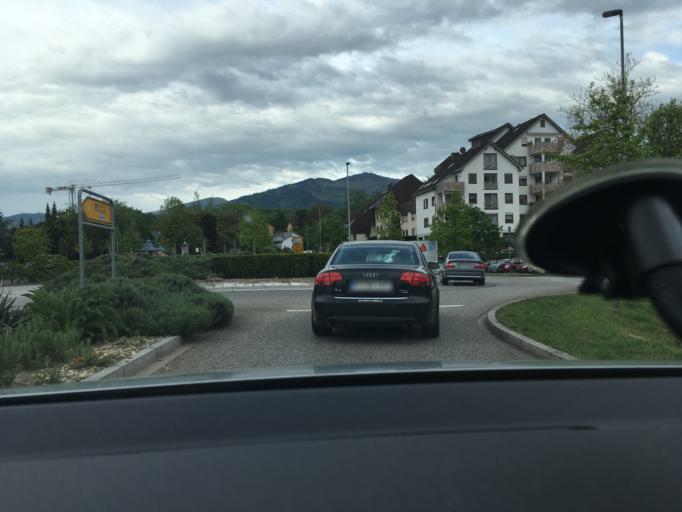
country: DE
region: Baden-Wuerttemberg
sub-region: Freiburg Region
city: Mullheim
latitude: 47.8044
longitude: 7.6255
